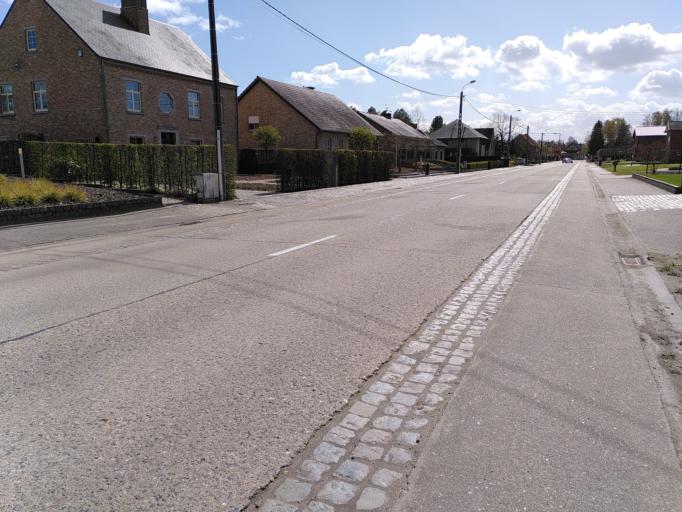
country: BE
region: Flanders
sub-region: Provincie Vlaams-Brabant
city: Begijnendijk
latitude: 51.0283
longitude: 4.8137
